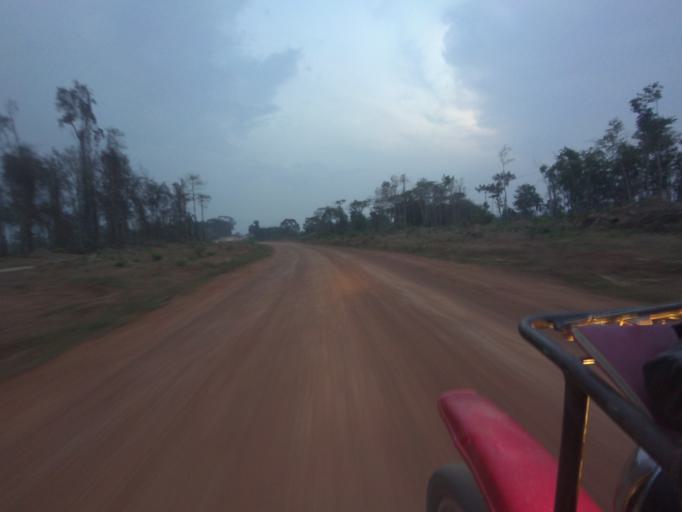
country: LR
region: Nimba
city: Sanniquellie
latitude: 7.2700
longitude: -8.8424
